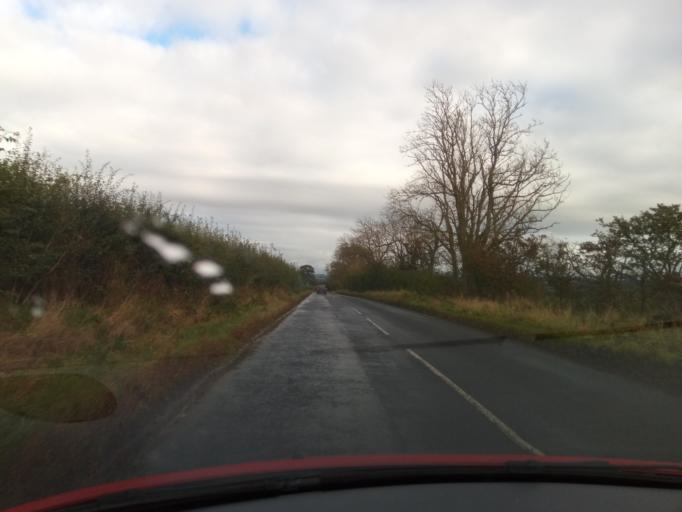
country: GB
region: Scotland
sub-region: The Scottish Borders
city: Newtown St Boswells
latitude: 55.5625
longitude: -2.6905
